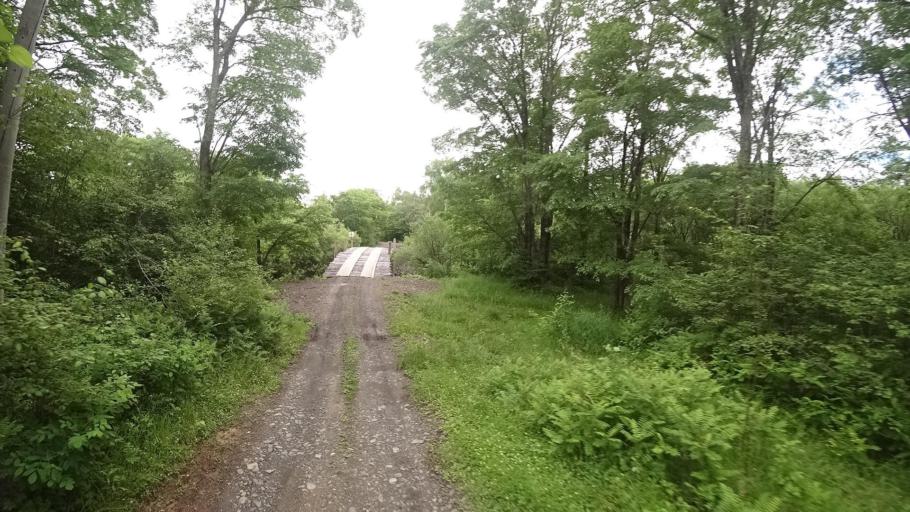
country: RU
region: Khabarovsk Krai
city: Amursk
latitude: 49.9048
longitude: 136.1326
